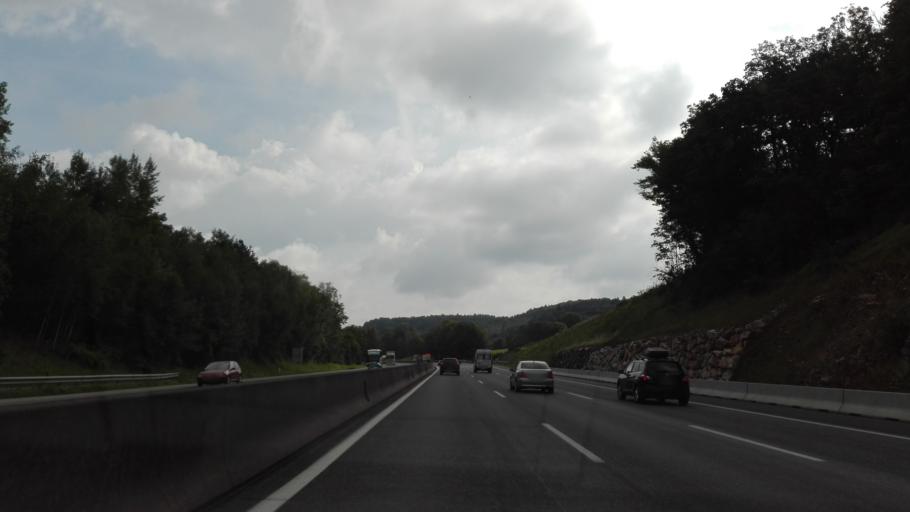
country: AT
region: Lower Austria
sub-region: Politischer Bezirk Melk
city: Erlauf
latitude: 48.1715
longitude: 15.1785
